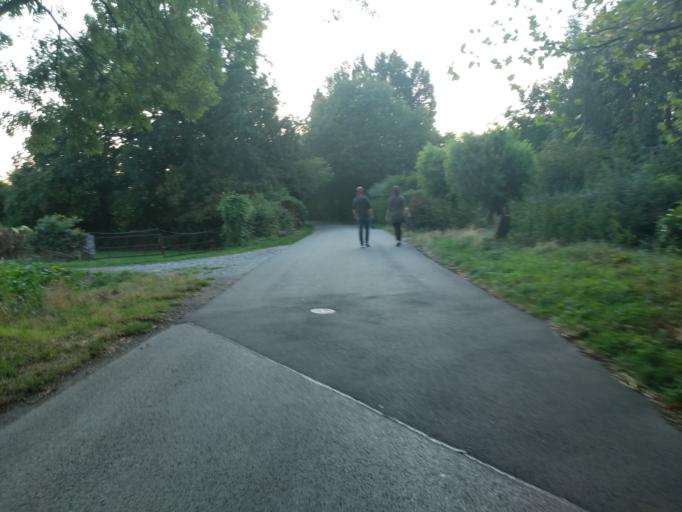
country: DE
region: North Rhine-Westphalia
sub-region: Regierungsbezirk Dusseldorf
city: Krefeld
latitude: 51.3312
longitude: 6.6398
